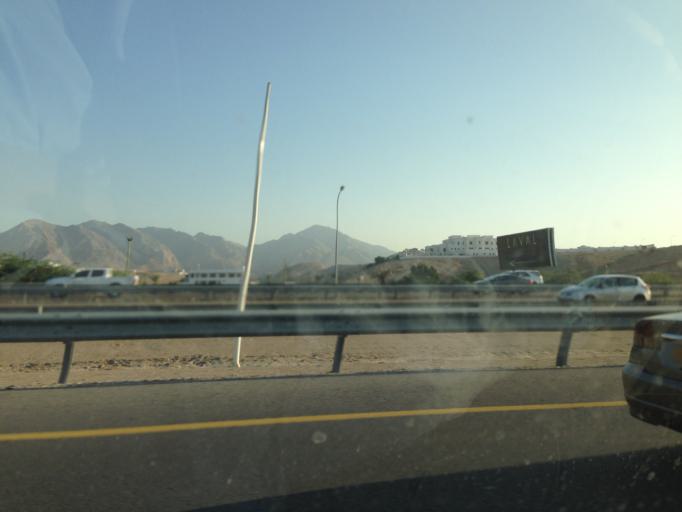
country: OM
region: Muhafazat Masqat
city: Bawshar
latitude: 23.5637
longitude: 58.3902
